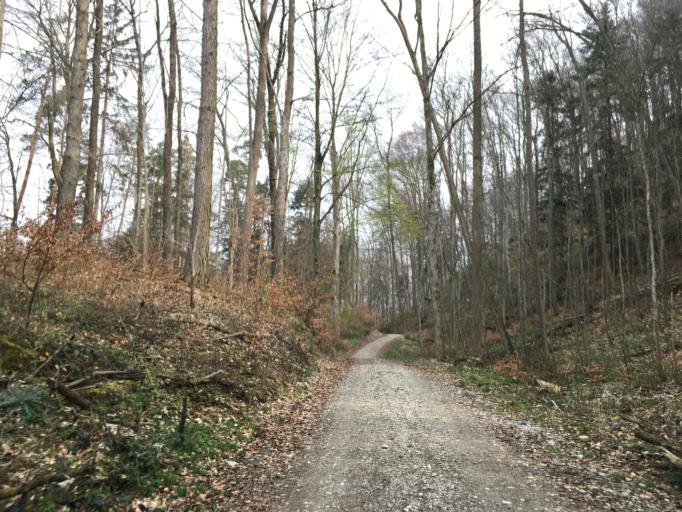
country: DE
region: Bavaria
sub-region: Upper Bavaria
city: Jettenbach
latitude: 48.1627
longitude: 12.3731
